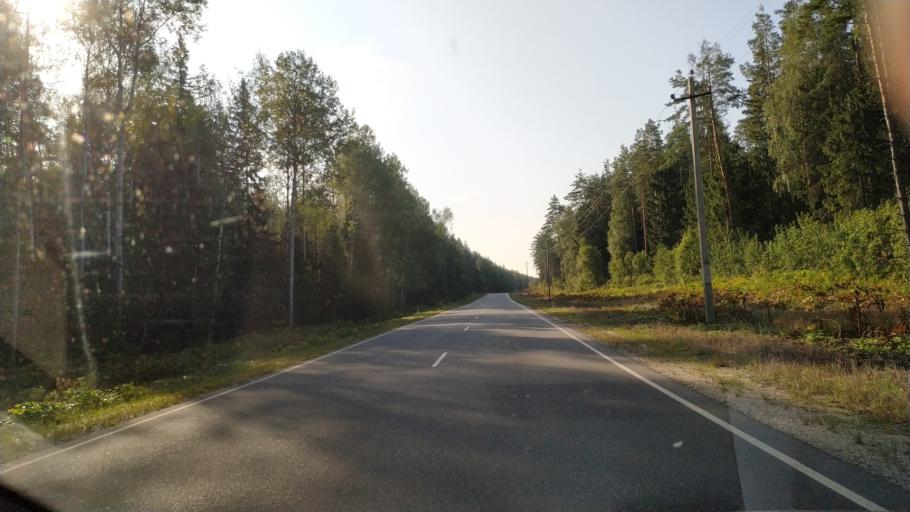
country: RU
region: Moskovskaya
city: Dmitrovskiy Pogost
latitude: 55.4251
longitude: 39.7358
